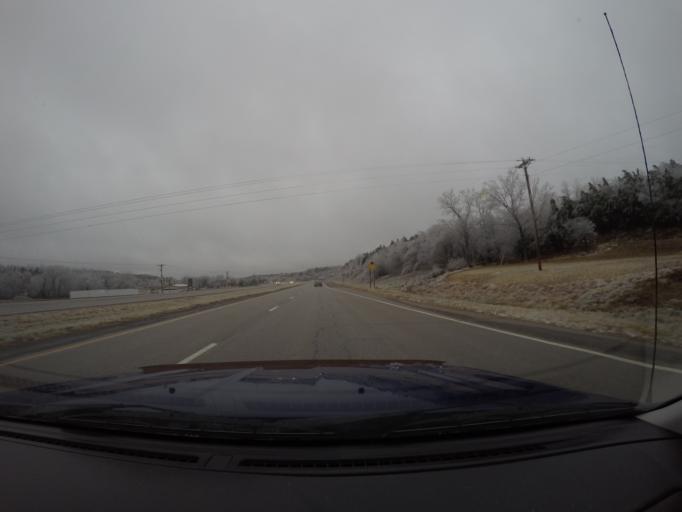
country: US
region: Kansas
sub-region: Riley County
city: Manhattan
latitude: 39.1557
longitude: -96.5382
